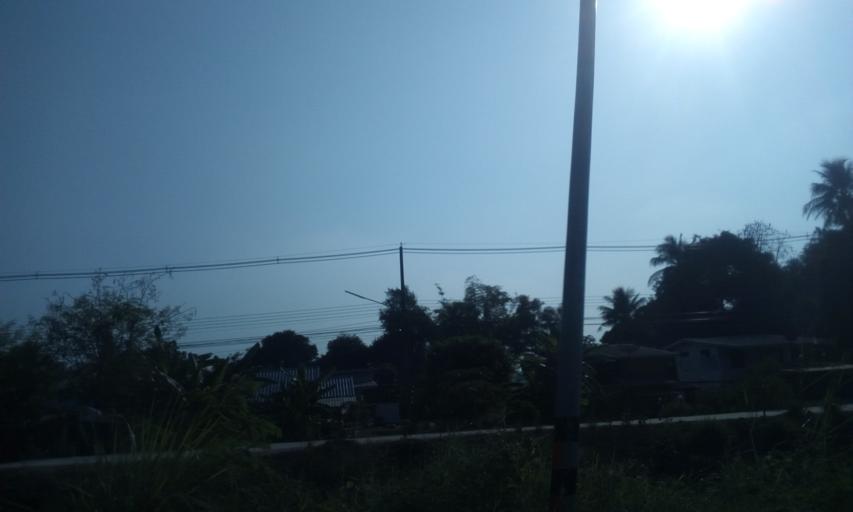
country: TH
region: Sing Buri
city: Sing Buri
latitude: 14.8471
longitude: 100.4198
